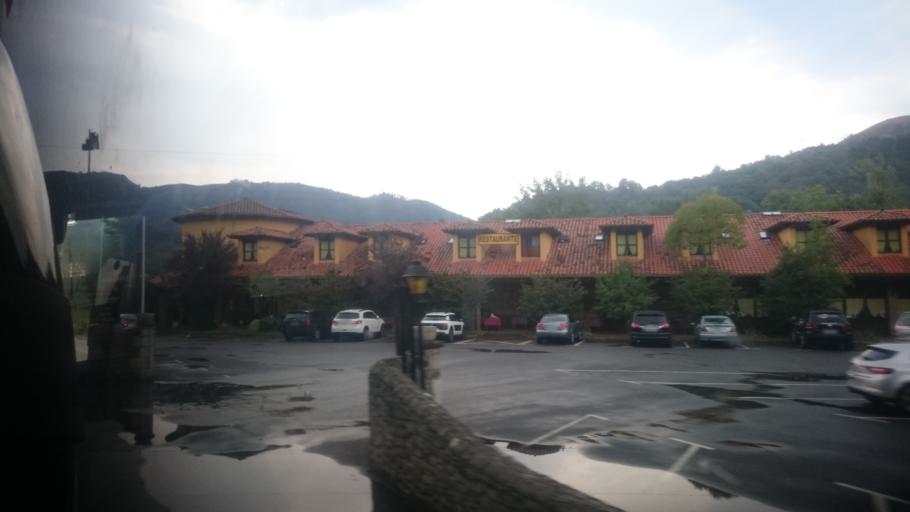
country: ES
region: Asturias
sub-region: Province of Asturias
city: Cangas de Onis
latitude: 43.3455
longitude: -5.0852
